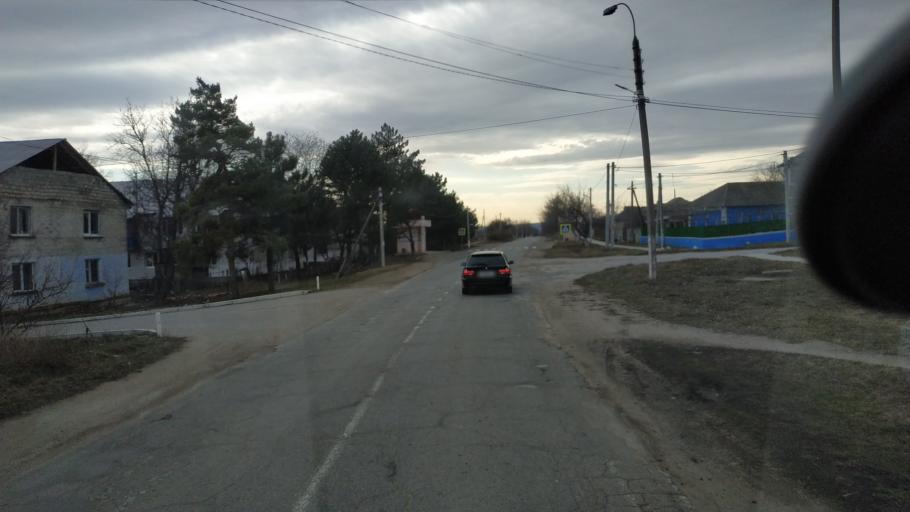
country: MD
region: Criuleni
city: Criuleni
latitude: 47.1617
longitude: 29.1187
